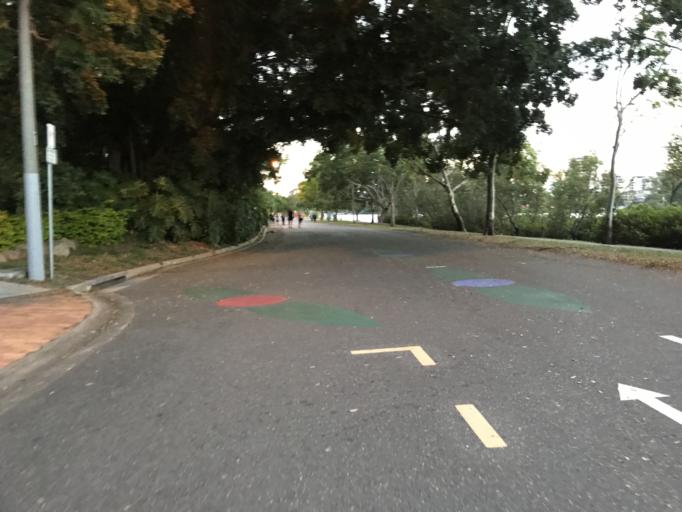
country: AU
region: Queensland
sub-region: Brisbane
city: Milton
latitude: -27.4793
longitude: 153.0025
